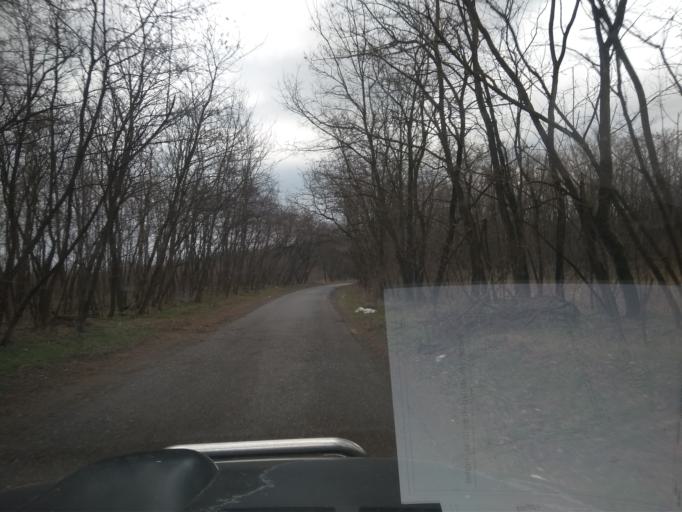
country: HU
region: Szabolcs-Szatmar-Bereg
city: Nyirpazony
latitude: 48.0231
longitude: 21.8025
